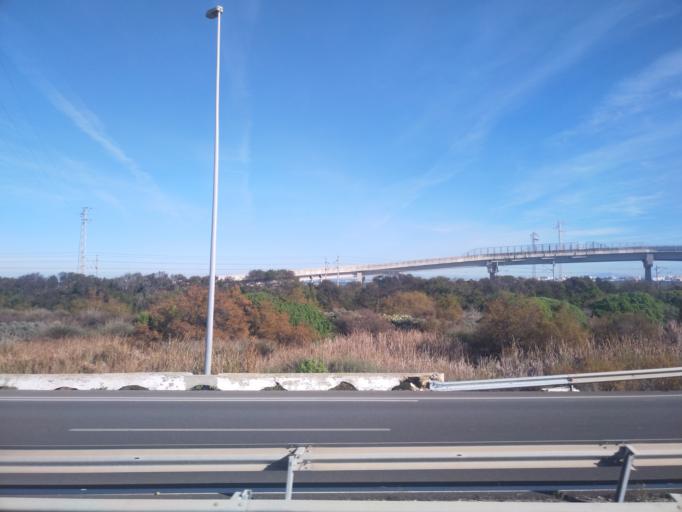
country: ES
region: Andalusia
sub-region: Provincia de Cadiz
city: San Fernando
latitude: 36.4620
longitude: -6.2516
